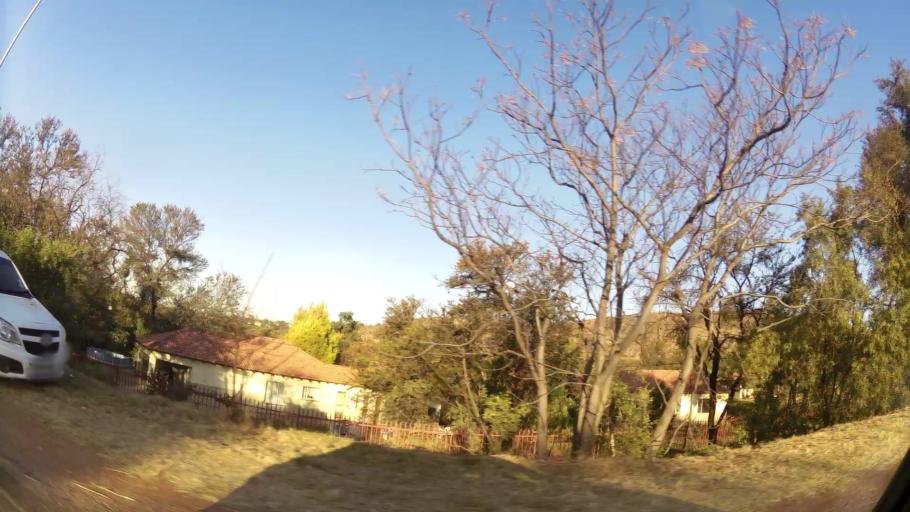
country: ZA
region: North-West
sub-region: Bojanala Platinum District Municipality
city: Rustenburg
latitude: -25.7153
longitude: 27.2394
